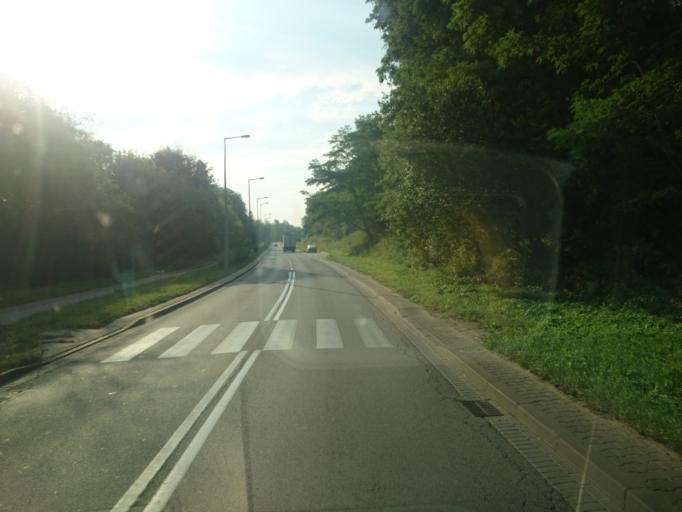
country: PL
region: Lubusz
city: Gorzow Wielkopolski
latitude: 52.7549
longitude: 15.2749
